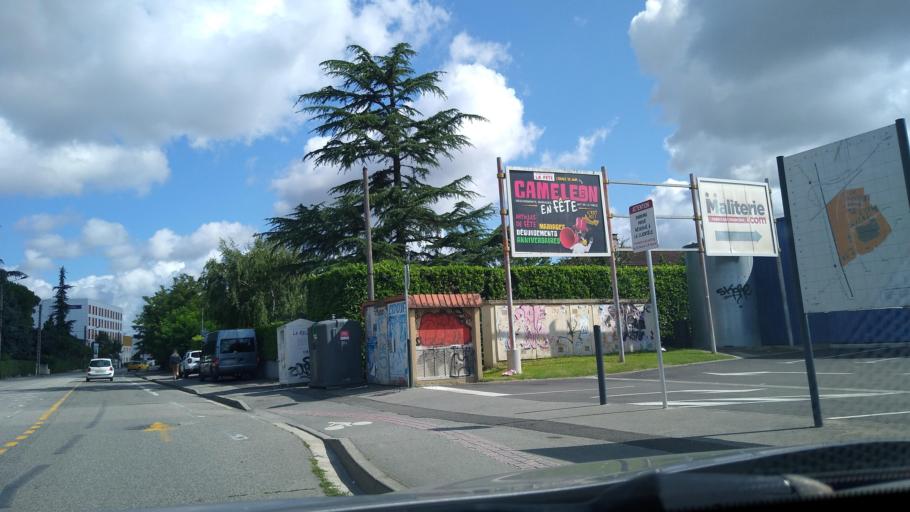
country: FR
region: Midi-Pyrenees
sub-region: Departement de la Haute-Garonne
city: Balma
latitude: 43.6326
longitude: 1.4820
